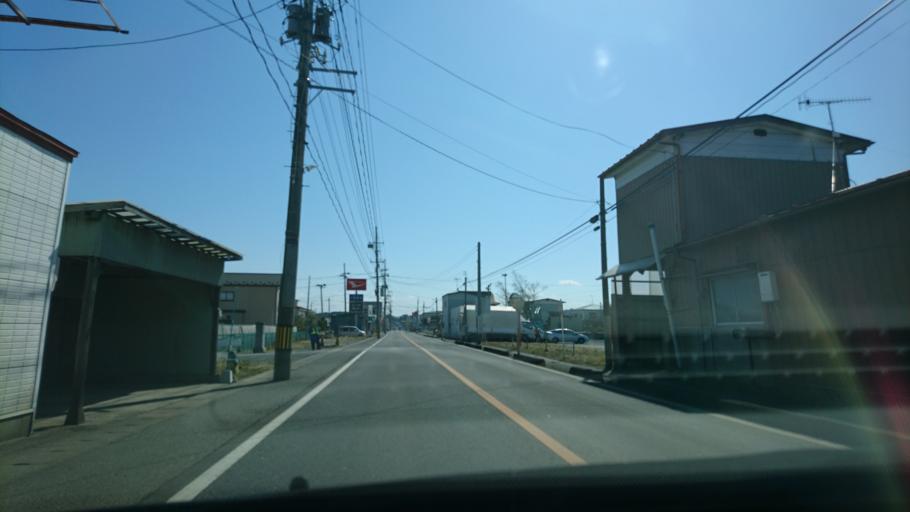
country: JP
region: Iwate
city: Ichinoseki
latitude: 38.7706
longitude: 141.1491
